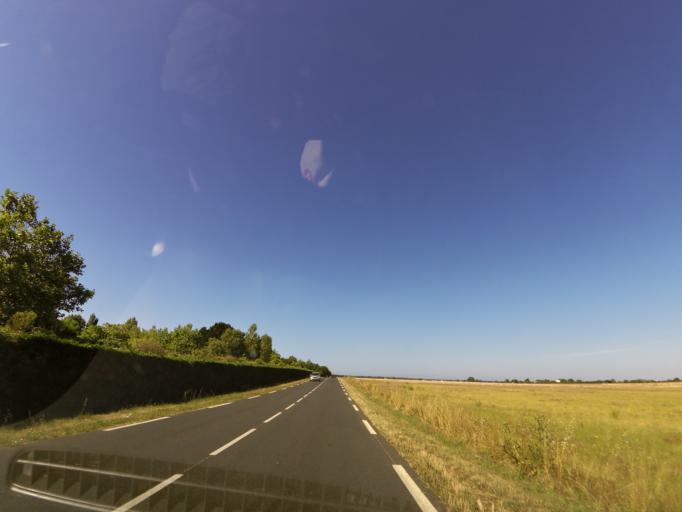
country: FR
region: Pays de la Loire
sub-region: Departement de la Vendee
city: Longeville-sur-Mer
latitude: 46.4197
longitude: -1.5273
